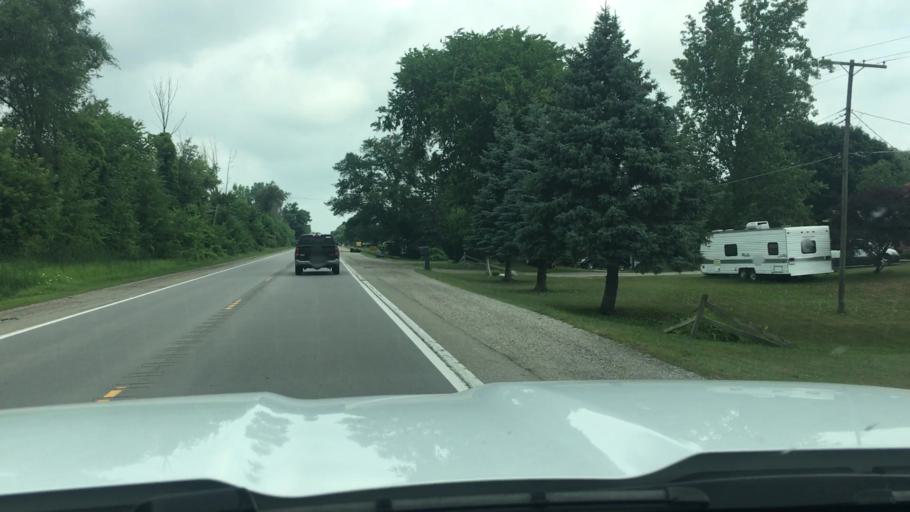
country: US
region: Michigan
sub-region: Lapeer County
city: Imlay City
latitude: 43.0395
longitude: -83.0720
